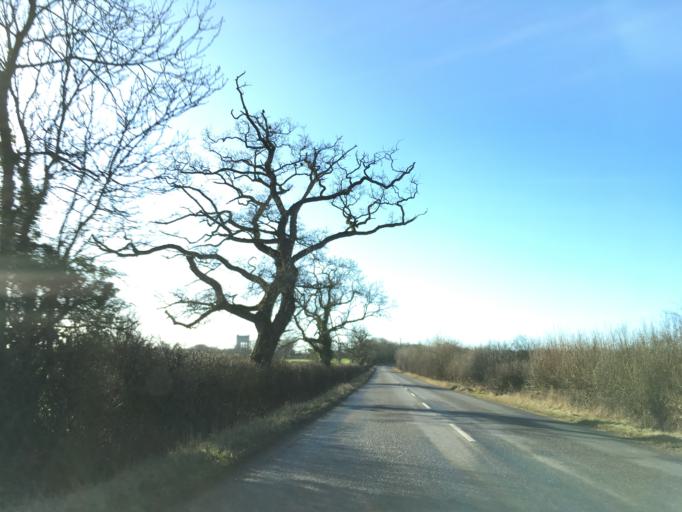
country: GB
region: England
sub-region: Wiltshire
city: Minety
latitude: 51.6025
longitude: -1.9843
